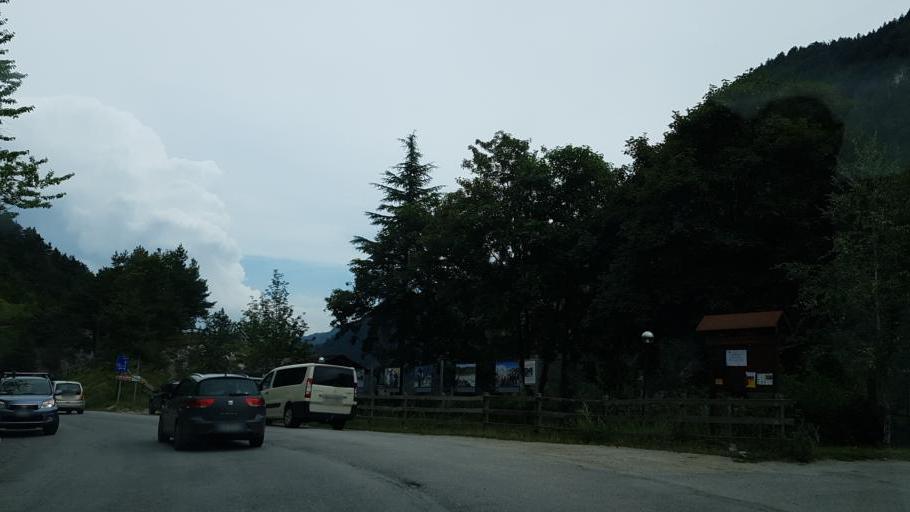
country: IT
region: Piedmont
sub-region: Provincia di Cuneo
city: Stroppo
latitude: 44.5030
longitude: 7.1336
